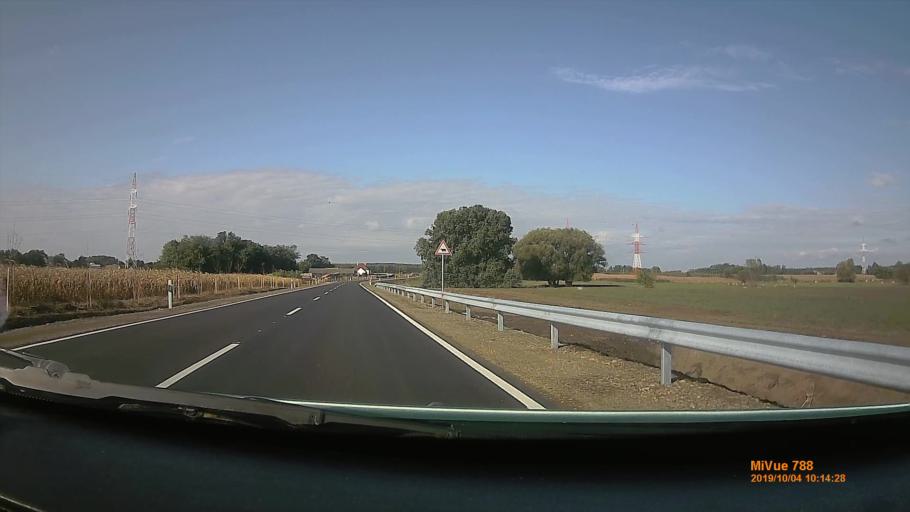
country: HU
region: Szabolcs-Szatmar-Bereg
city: Nyiregyhaza
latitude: 47.9417
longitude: 21.6688
